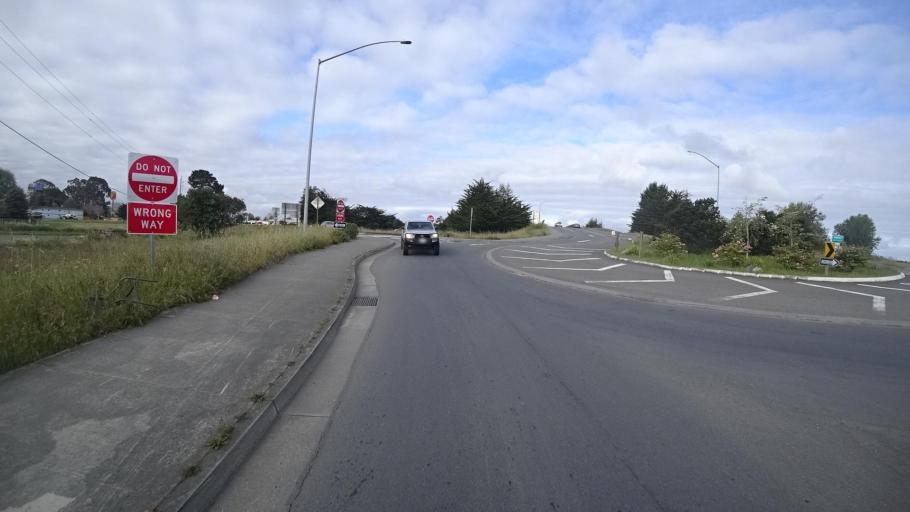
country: US
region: California
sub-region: Humboldt County
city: Arcata
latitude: 40.9048
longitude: -124.0848
